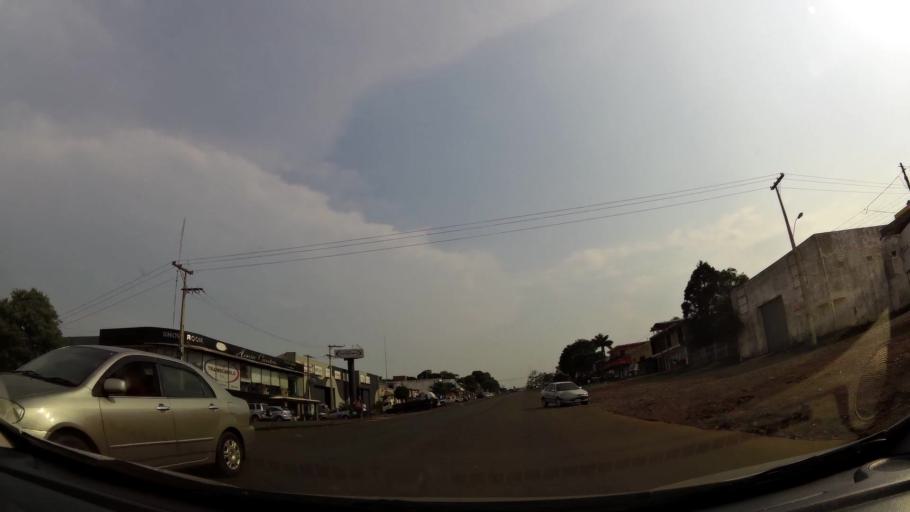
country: PY
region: Alto Parana
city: Ciudad del Este
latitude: -25.4943
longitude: -54.6618
